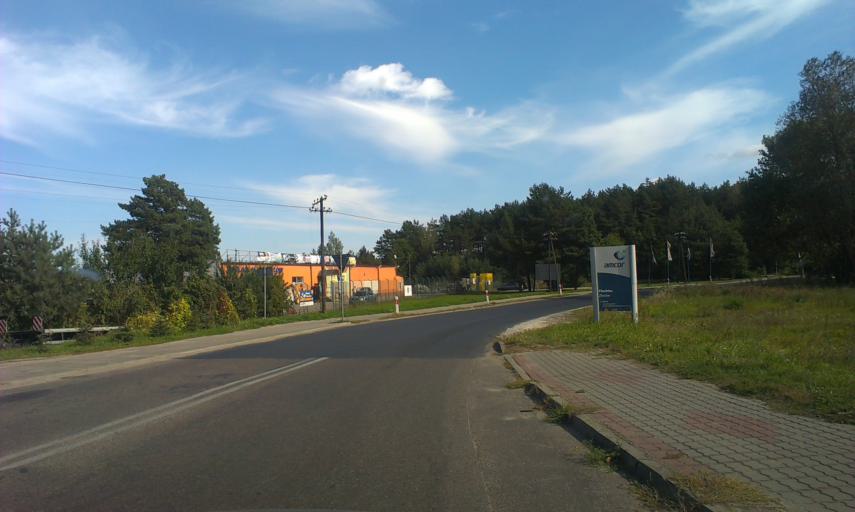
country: PL
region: Greater Poland Voivodeship
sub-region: Powiat zlotowski
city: Zlotow
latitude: 53.3540
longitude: 17.0510
